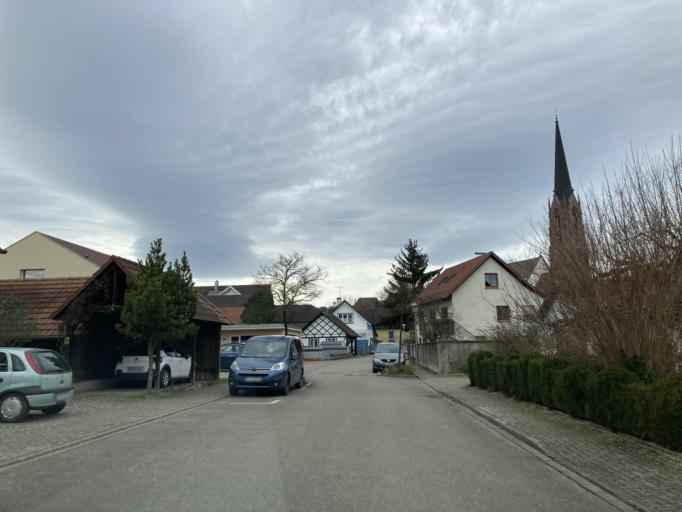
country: DE
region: Baden-Wuerttemberg
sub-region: Freiburg Region
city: Eichstetten
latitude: 48.0931
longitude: 7.7473
